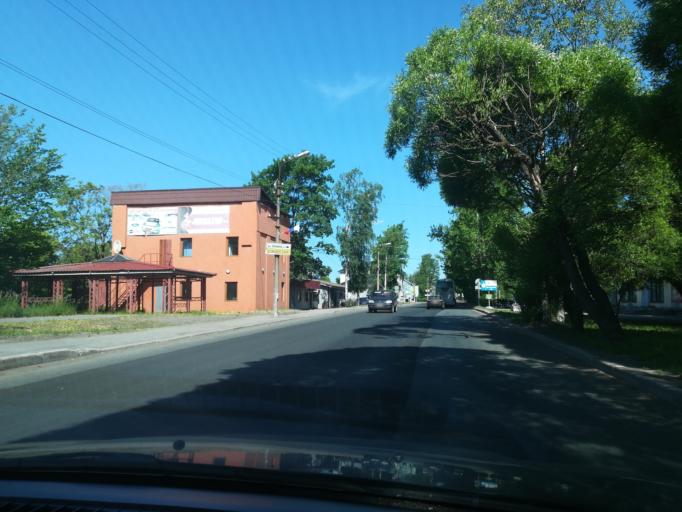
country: RU
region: Leningrad
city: Svetogorsk
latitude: 61.1132
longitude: 28.8552
